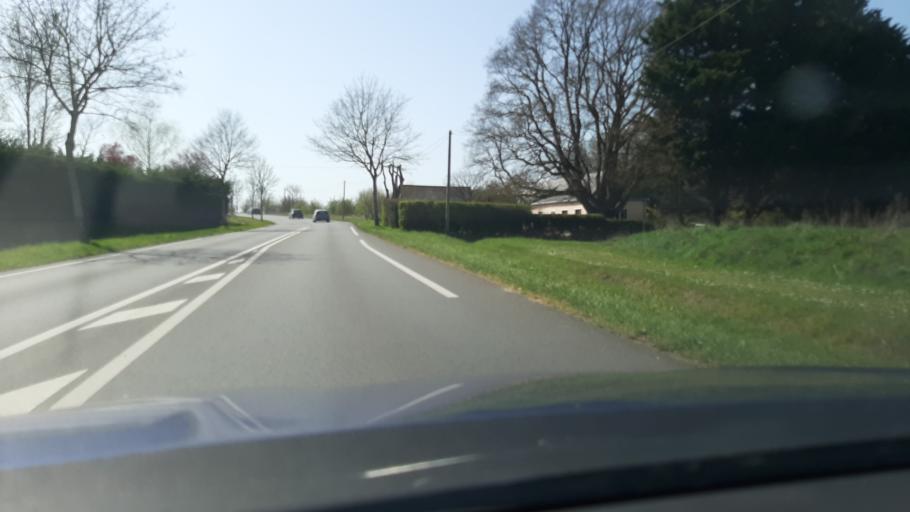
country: FR
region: Pays de la Loire
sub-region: Departement de Maine-et-Loire
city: Pellouailles-les-Vignes
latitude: 47.5086
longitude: -0.4795
